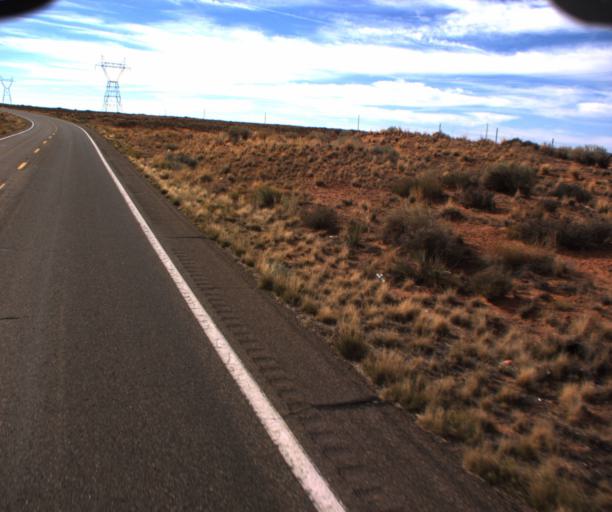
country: US
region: Arizona
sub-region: Coconino County
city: LeChee
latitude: 36.8578
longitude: -111.3374
